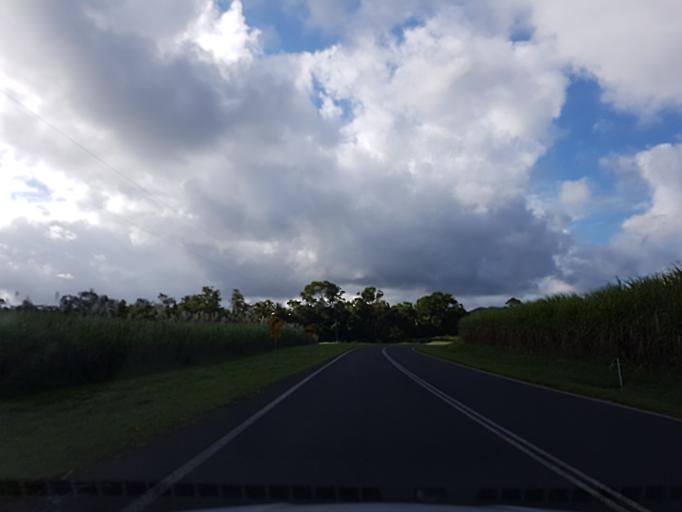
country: AU
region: Queensland
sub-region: Cairns
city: Port Douglas
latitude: -16.2805
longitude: 145.3797
